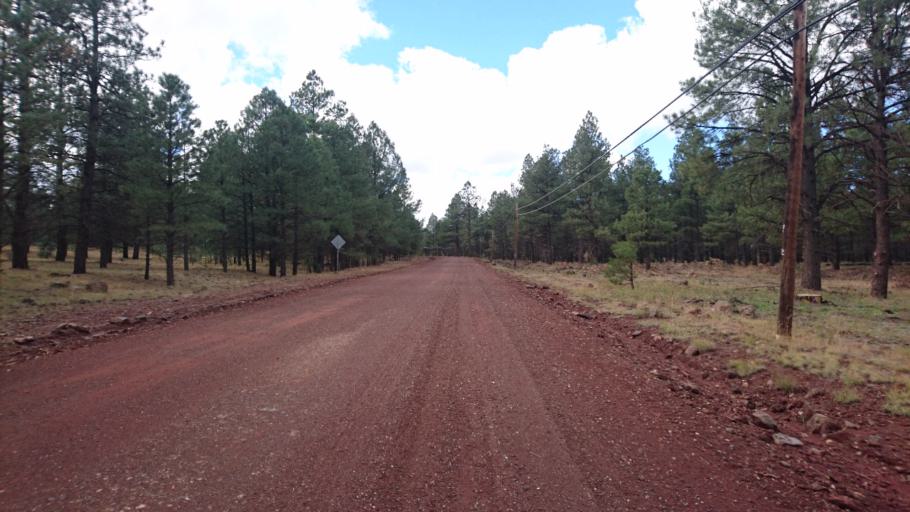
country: US
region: Arizona
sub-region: Coconino County
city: Williams
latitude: 35.2651
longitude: -112.0850
